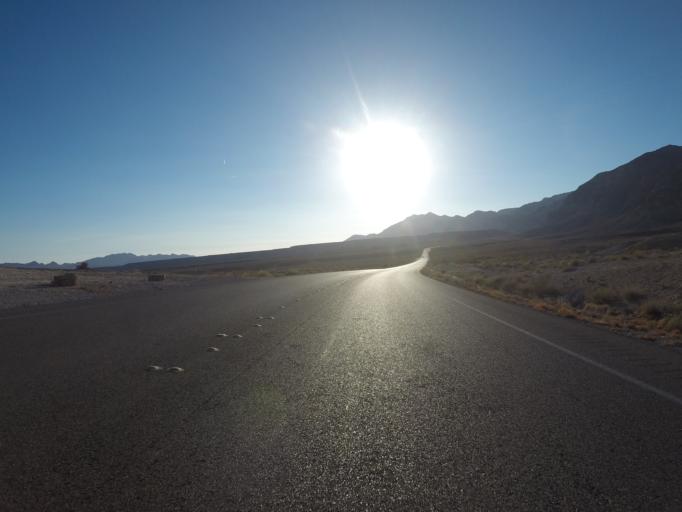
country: US
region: Nevada
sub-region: Clark County
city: Moapa Valley
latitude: 36.3698
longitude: -114.4452
